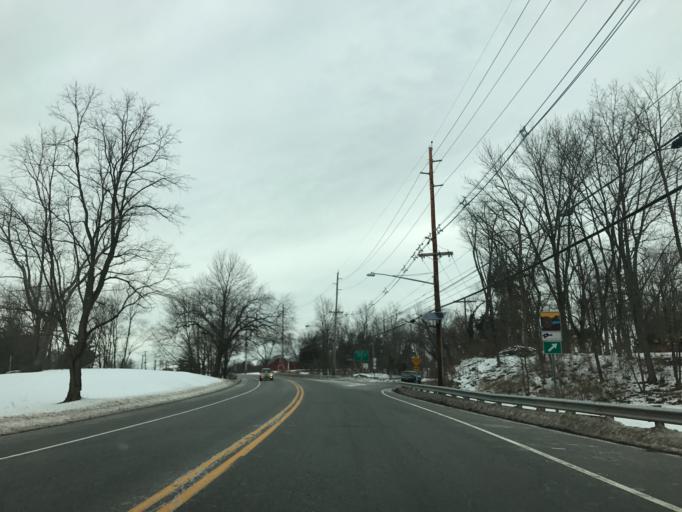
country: US
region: New Jersey
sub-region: Somerset County
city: Ten Mile Run
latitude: 40.4150
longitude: -74.6504
